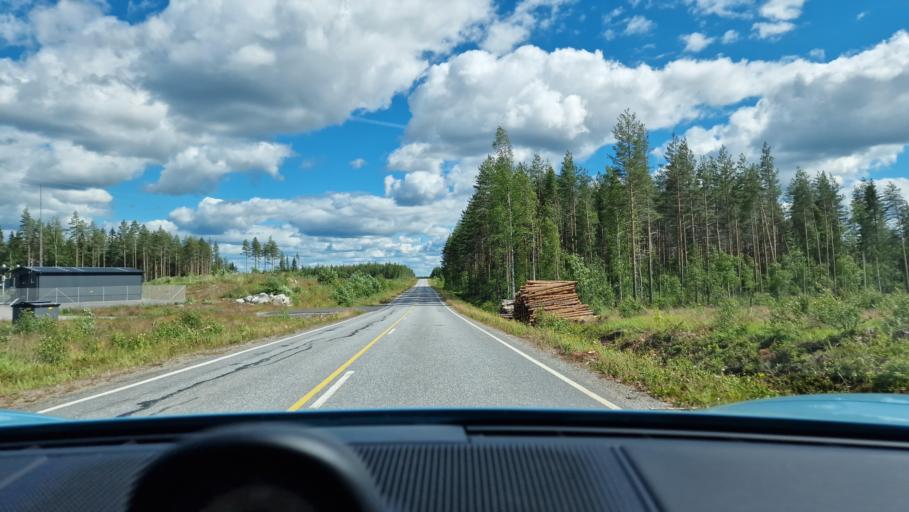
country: FI
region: Central Finland
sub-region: Saarijaervi-Viitasaari
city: Pylkoenmaeki
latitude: 62.6639
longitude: 24.5497
